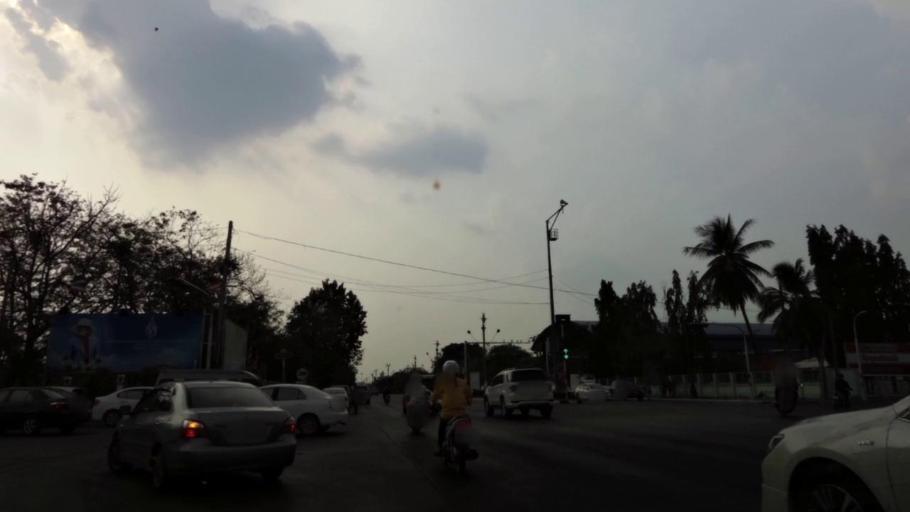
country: TH
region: Phra Nakhon Si Ayutthaya
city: Phra Nakhon Si Ayutthaya
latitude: 14.3664
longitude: 100.5591
